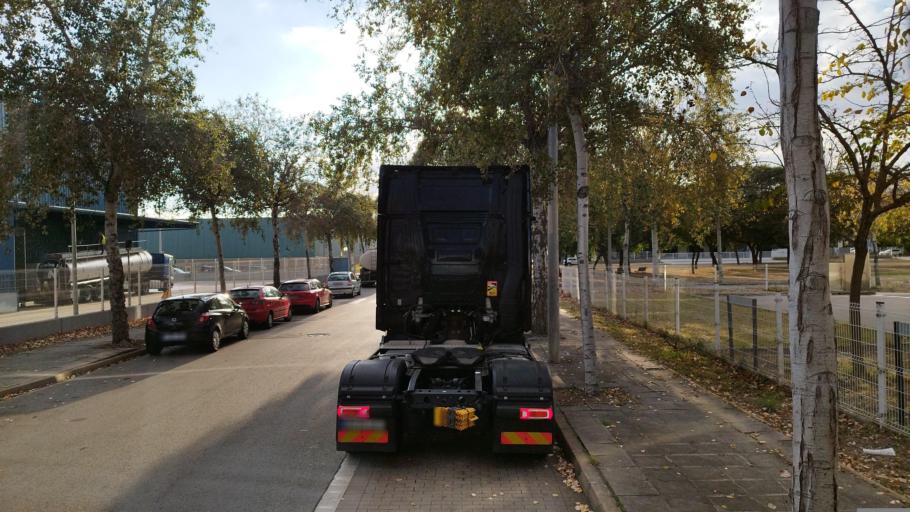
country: ES
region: Catalonia
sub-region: Provincia de Barcelona
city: Gava
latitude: 41.2866
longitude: 1.9949
